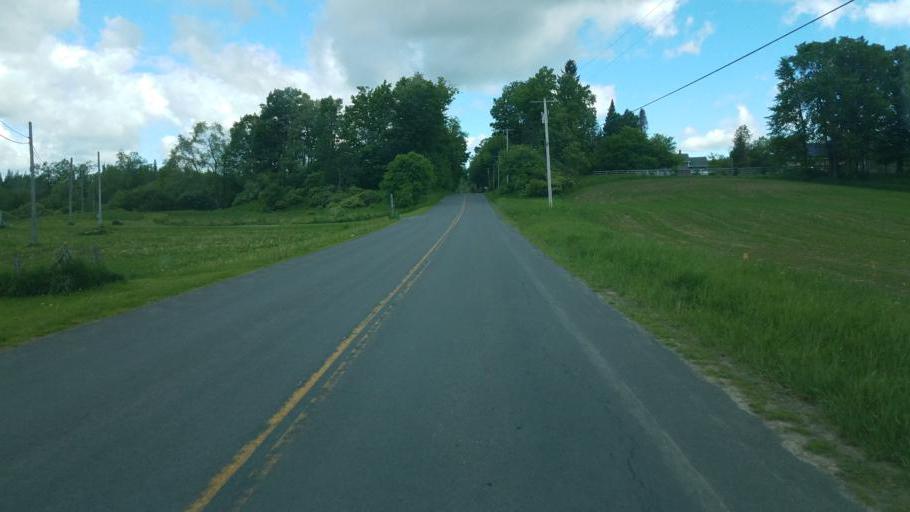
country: US
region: New York
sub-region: Oneida County
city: Boonville
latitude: 43.3419
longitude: -75.1917
